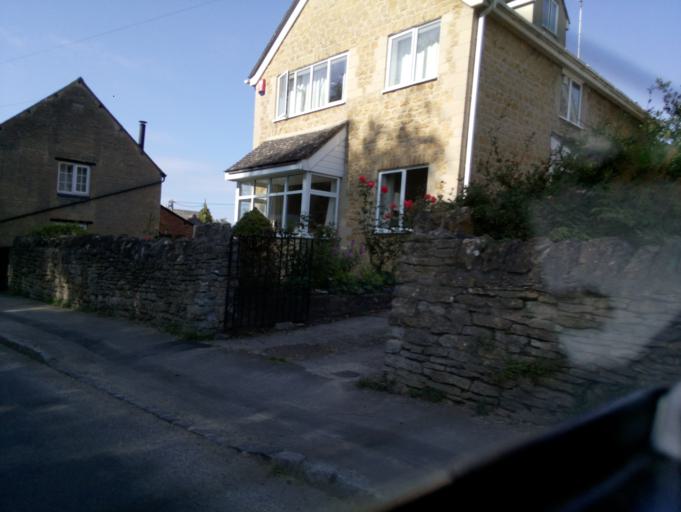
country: GB
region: England
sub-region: Oxfordshire
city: Carterton
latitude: 51.7141
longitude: -1.5893
